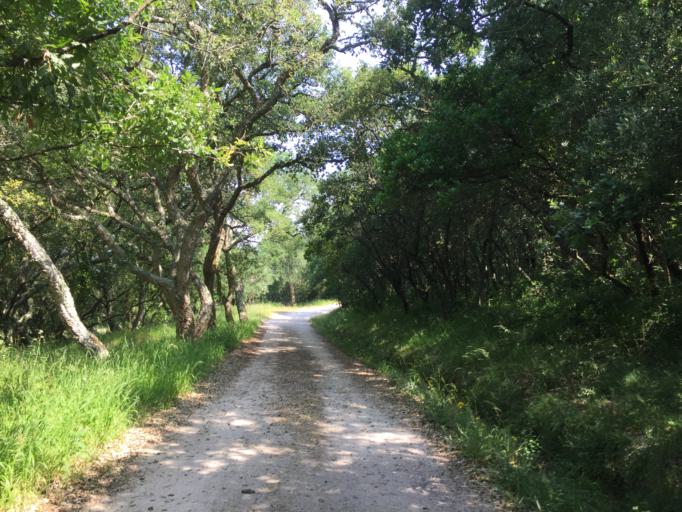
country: PT
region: Lisbon
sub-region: Mafra
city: Milharado
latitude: 38.9047
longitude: -9.1870
